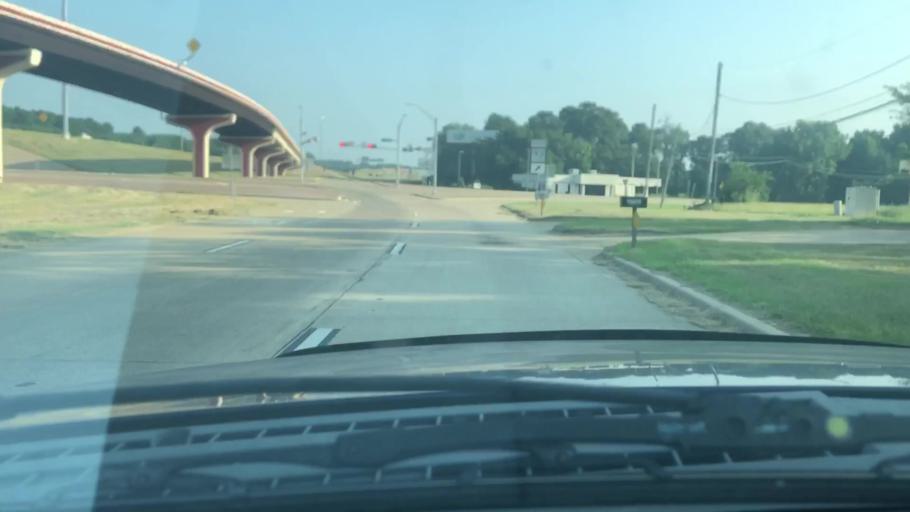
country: US
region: Texas
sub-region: Bowie County
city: Wake Village
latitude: 33.3944
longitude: -94.0968
